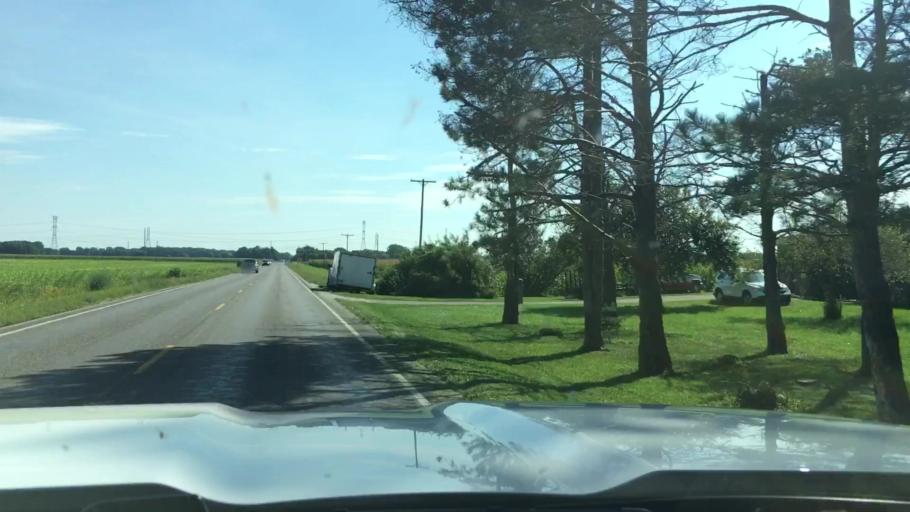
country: US
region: Michigan
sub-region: Saginaw County
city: Freeland
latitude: 43.5253
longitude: -84.1952
